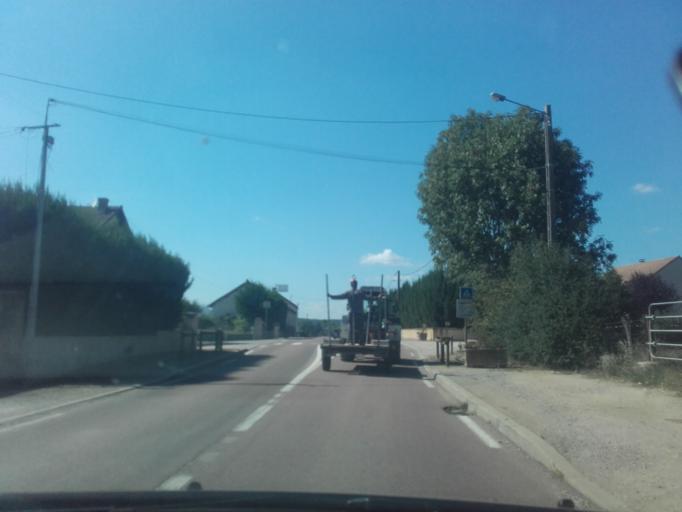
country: FR
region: Bourgogne
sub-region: Departement de la Cote-d'Or
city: Nolay
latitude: 46.9437
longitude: 4.6512
